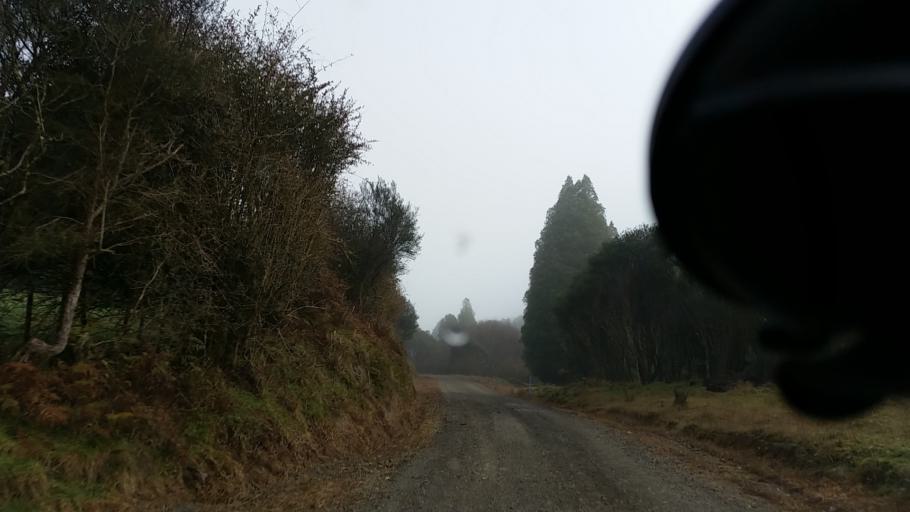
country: NZ
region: Taranaki
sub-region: New Plymouth District
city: Waitara
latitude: -38.9731
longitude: 174.8044
